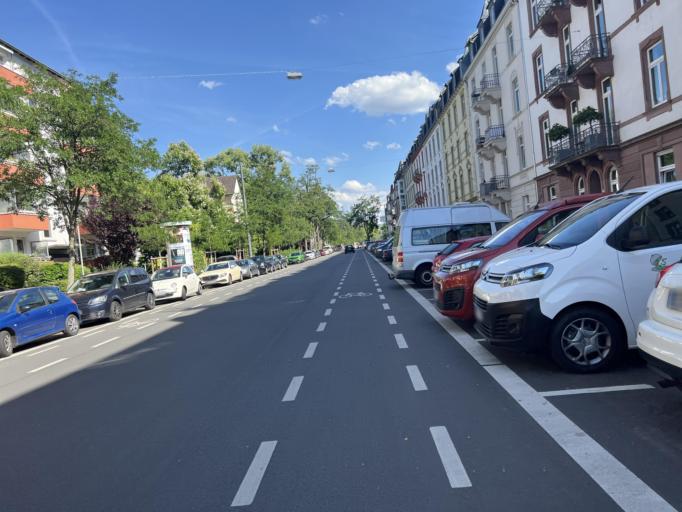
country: DE
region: Hesse
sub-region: Regierungsbezirk Darmstadt
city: Frankfurt am Main
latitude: 50.1271
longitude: 8.6432
